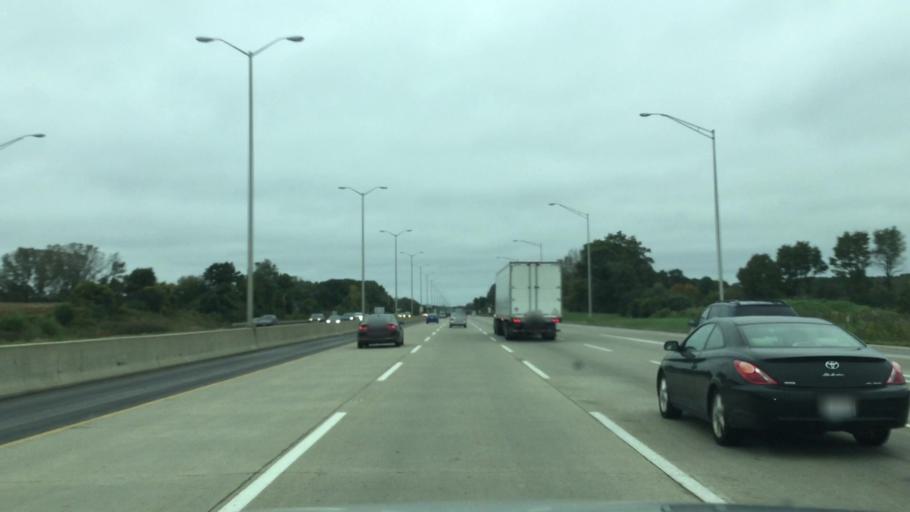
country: US
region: Illinois
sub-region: Lake County
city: Wadsworth
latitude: 42.4610
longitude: -87.9625
